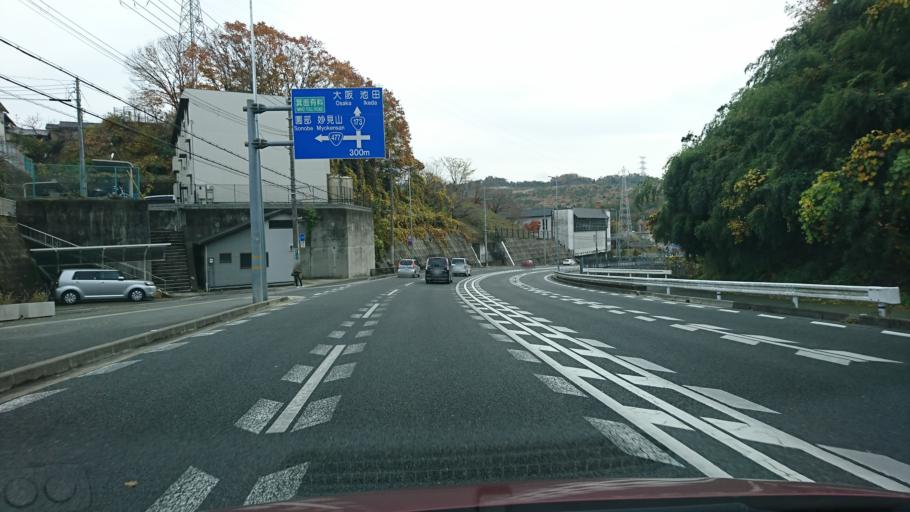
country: JP
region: Osaka
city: Ikeda
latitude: 34.8815
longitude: 135.4184
